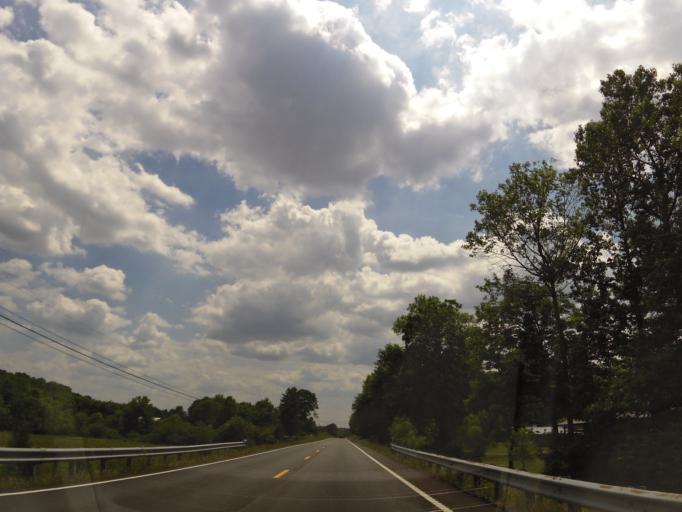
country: US
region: Tennessee
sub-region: Sequatchie County
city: Dunlap
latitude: 35.4723
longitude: -85.3182
